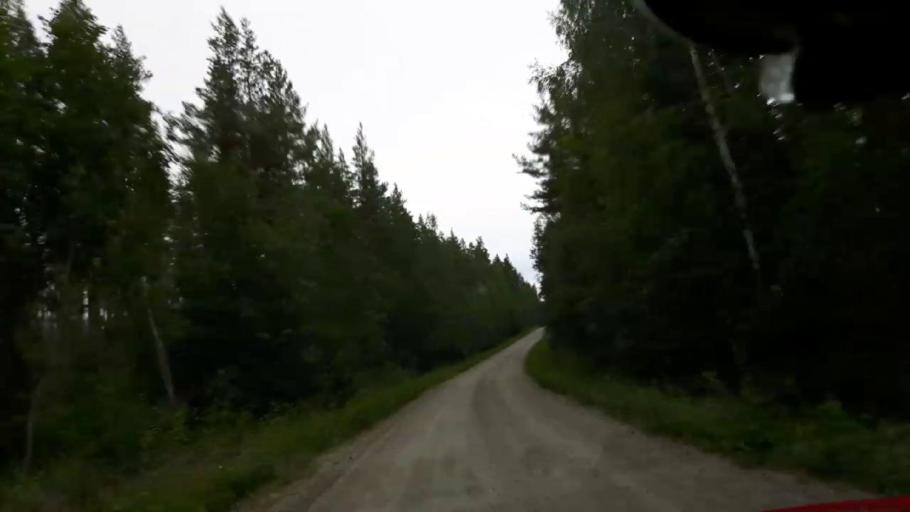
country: SE
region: Vaesternorrland
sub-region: Ange Kommun
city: Ange
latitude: 62.7918
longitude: 15.7732
